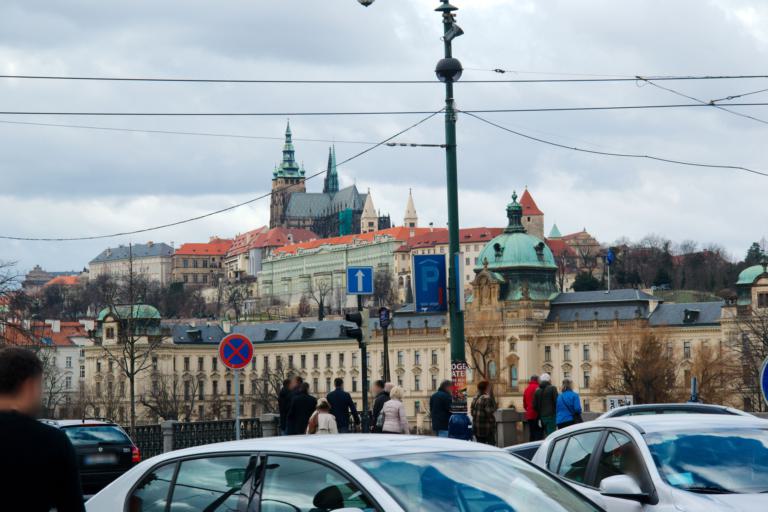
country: CZ
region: Praha
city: Prague
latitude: 50.0922
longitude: 14.4180
